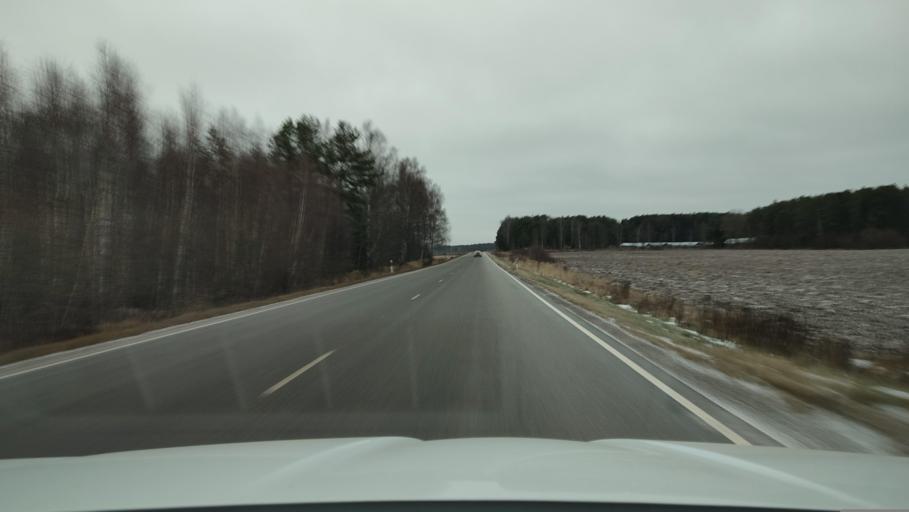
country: FI
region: Ostrobothnia
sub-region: Sydosterbotten
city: Naerpes
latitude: 62.5342
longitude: 21.4639
